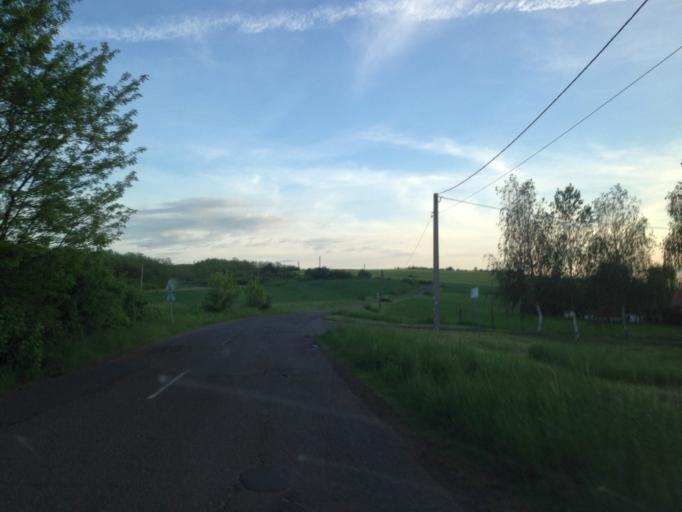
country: HU
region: Nograd
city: Tar
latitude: 47.9446
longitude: 19.7285
